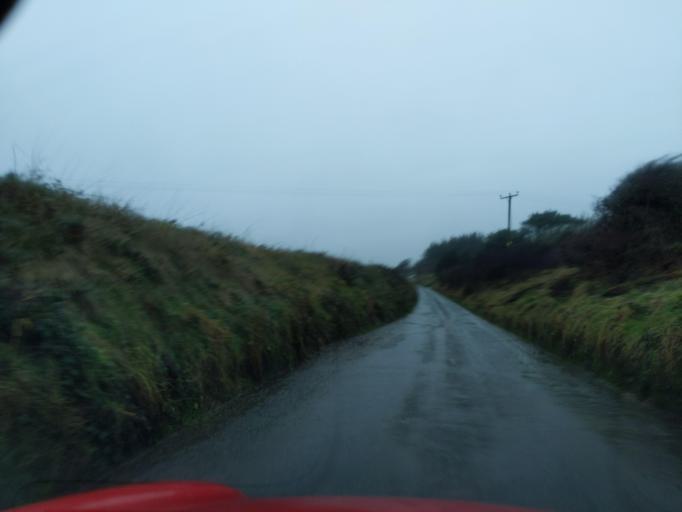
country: GB
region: England
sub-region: Cornwall
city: Camelford
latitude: 50.6475
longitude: -4.6993
